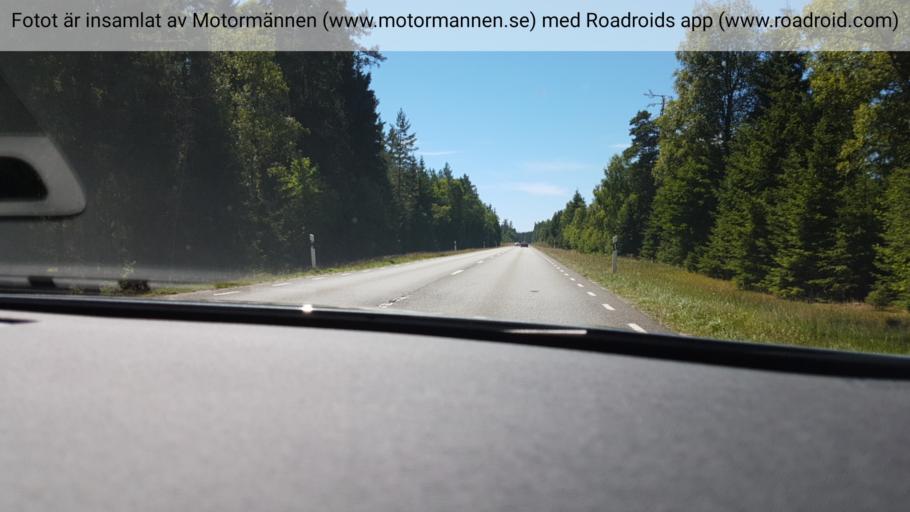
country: SE
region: Joenkoeping
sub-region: Gnosjo Kommun
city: Marieholm
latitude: 57.6385
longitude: 13.7961
